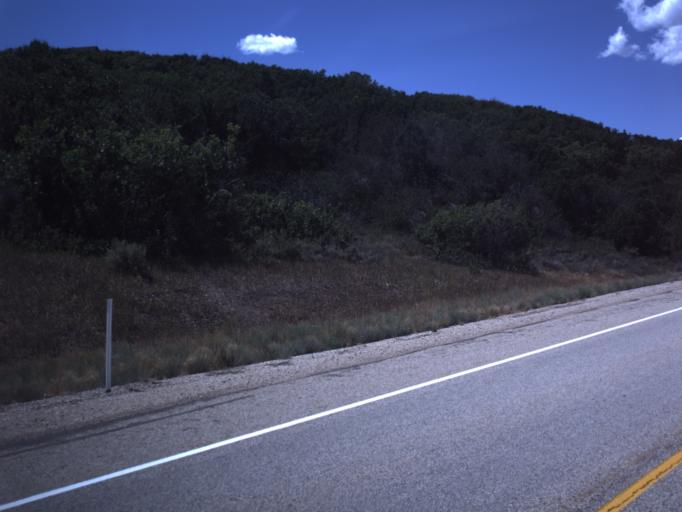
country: US
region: Utah
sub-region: Summit County
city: Francis
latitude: 40.5954
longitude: -111.3692
